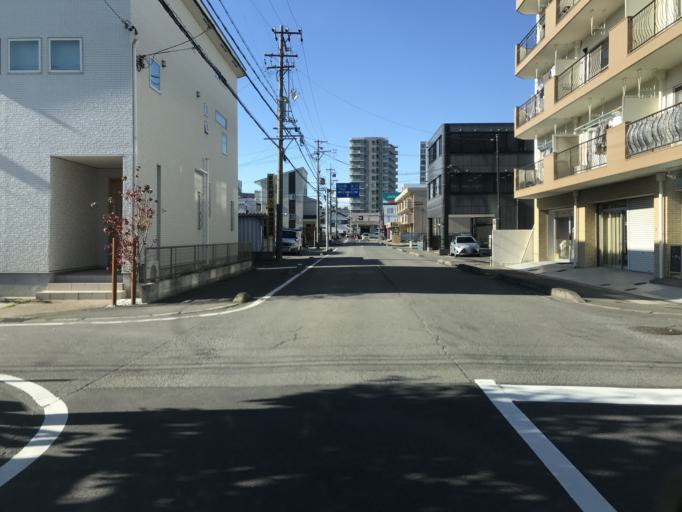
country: JP
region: Aichi
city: Nagoya-shi
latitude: 35.2007
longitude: 136.8645
